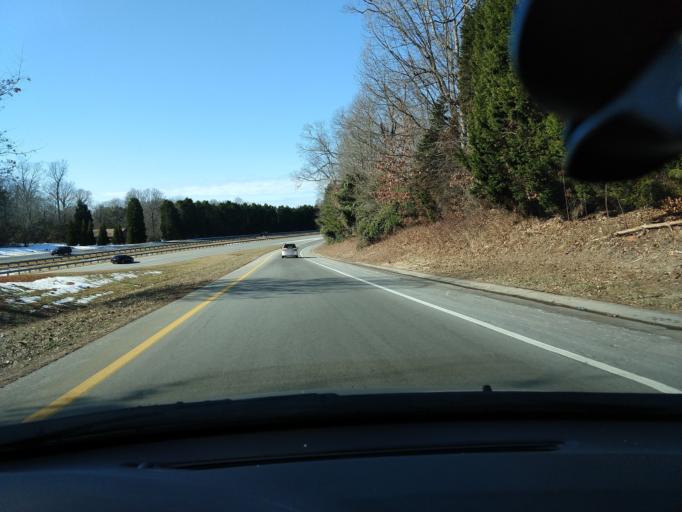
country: US
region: North Carolina
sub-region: Guilford County
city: Greensboro
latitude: 36.1139
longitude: -79.8515
